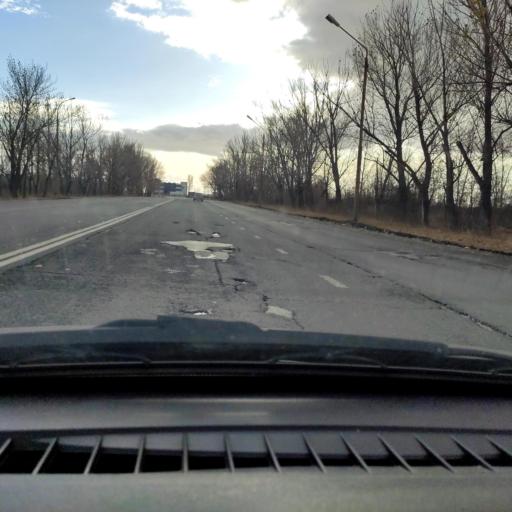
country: RU
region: Samara
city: Podstepki
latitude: 53.5632
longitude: 49.2160
